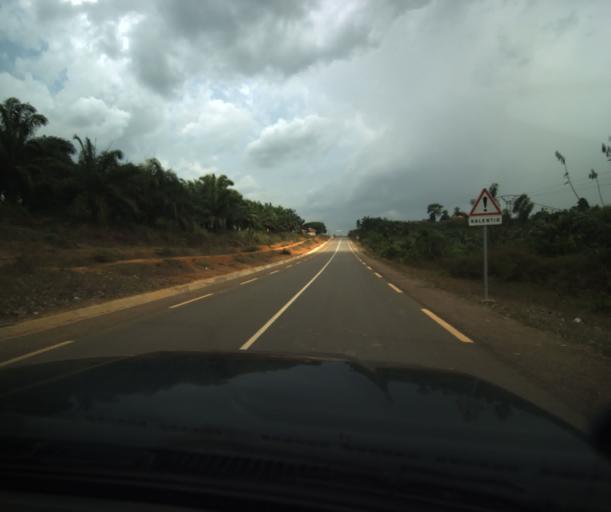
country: CM
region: Centre
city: Akono
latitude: 3.5055
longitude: 11.3257
